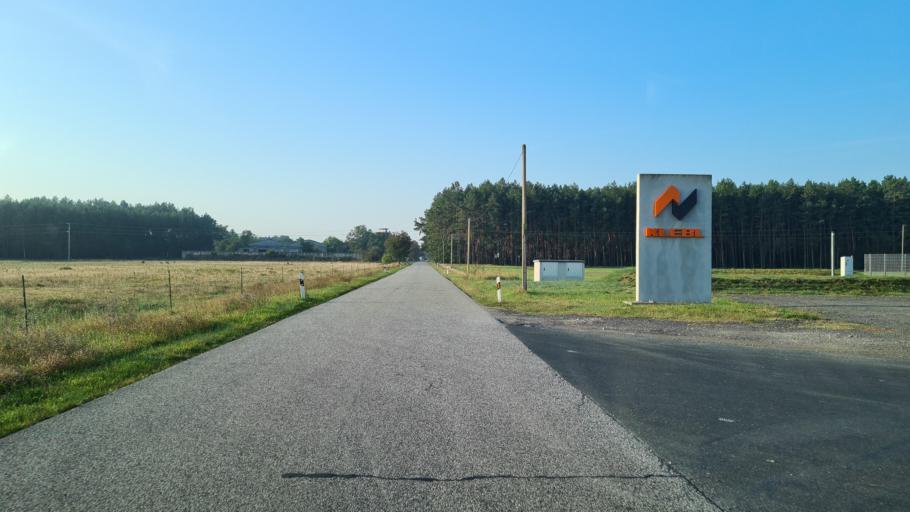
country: DE
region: Brandenburg
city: Luckenwalde
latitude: 52.1096
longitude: 13.0705
